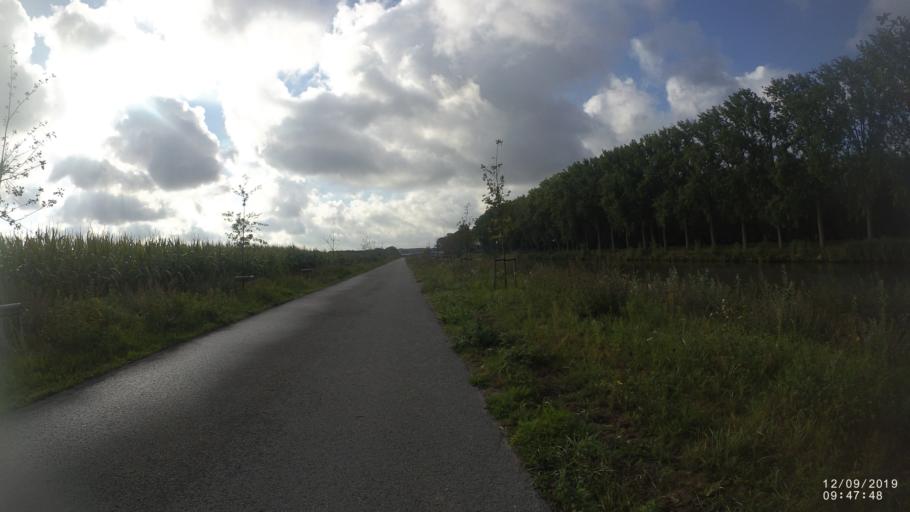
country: BE
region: Flanders
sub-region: Provincie Oost-Vlaanderen
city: Zomergem
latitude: 51.0797
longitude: 3.5648
